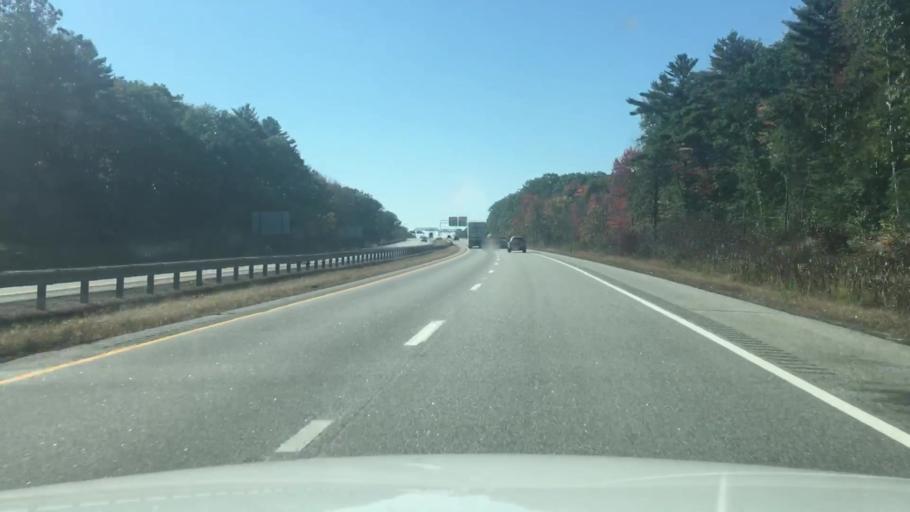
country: US
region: Maine
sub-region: Cumberland County
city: Falmouth
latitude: 43.7344
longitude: -70.2467
